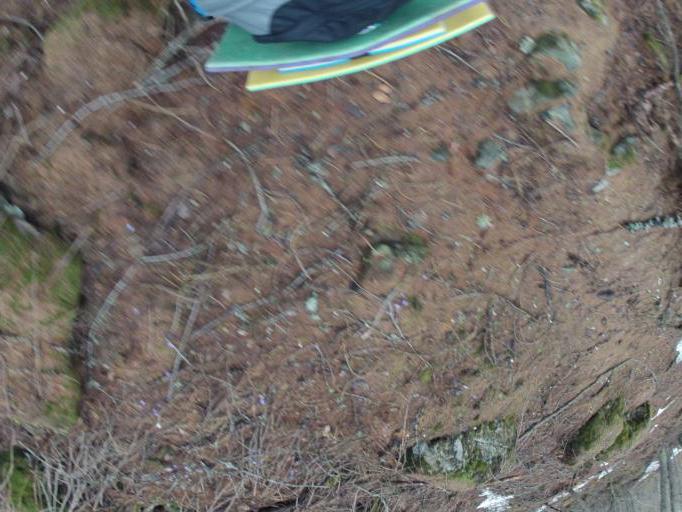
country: IT
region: Piedmont
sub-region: Provincia di Cuneo
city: Crissolo
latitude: 44.6999
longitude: 7.1423
